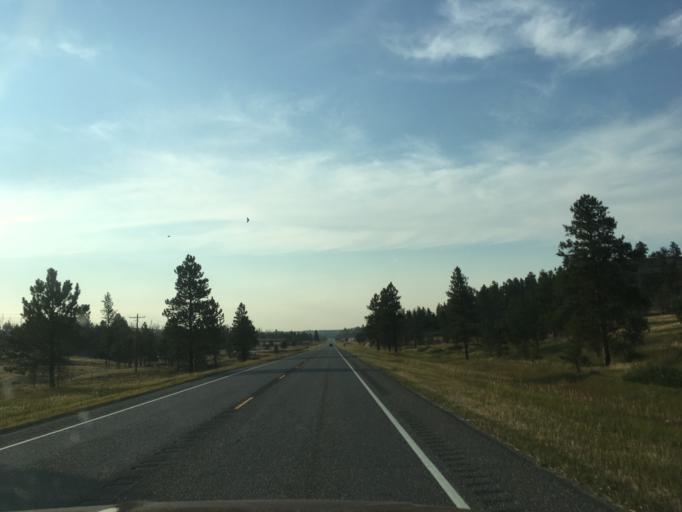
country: US
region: Montana
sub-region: Musselshell County
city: Roundup
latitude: 46.2815
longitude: -108.4770
